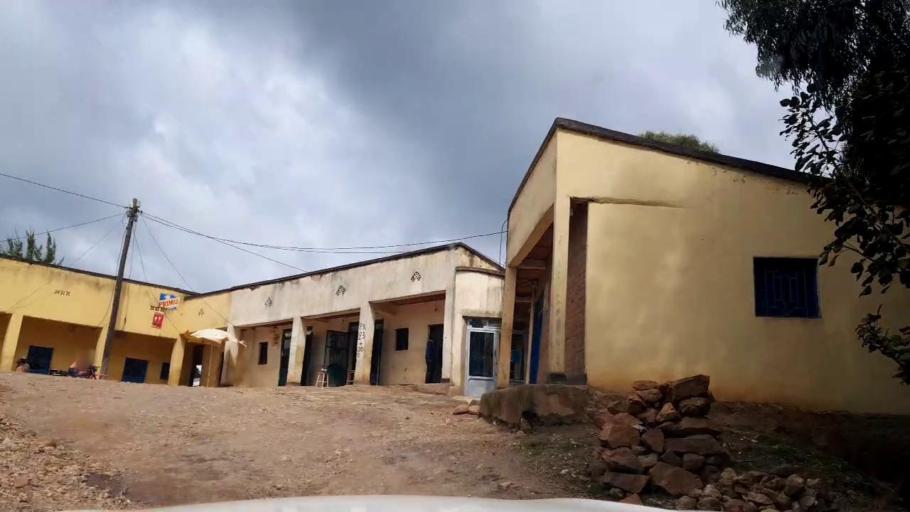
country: RW
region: Western Province
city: Kibuye
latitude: -1.8936
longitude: 29.4574
